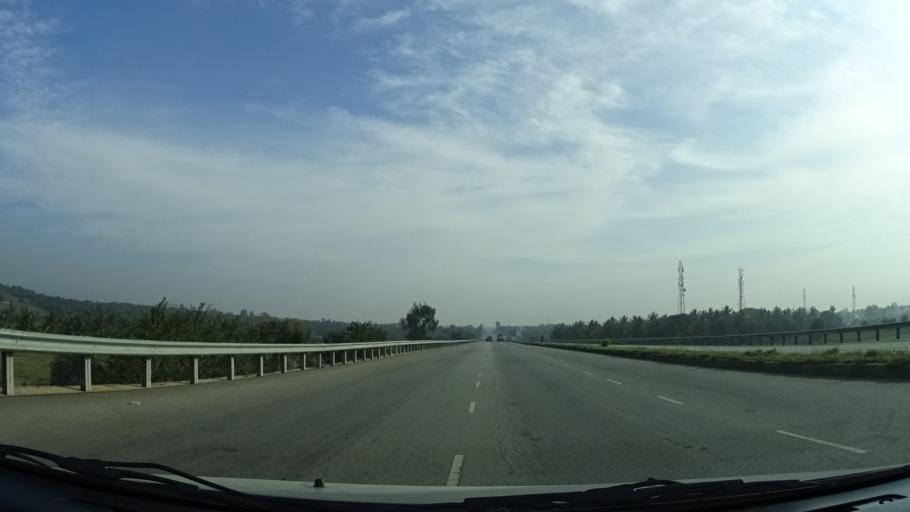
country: IN
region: Karnataka
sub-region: Bangalore Rural
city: Devanhalli
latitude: 13.2164
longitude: 77.6774
